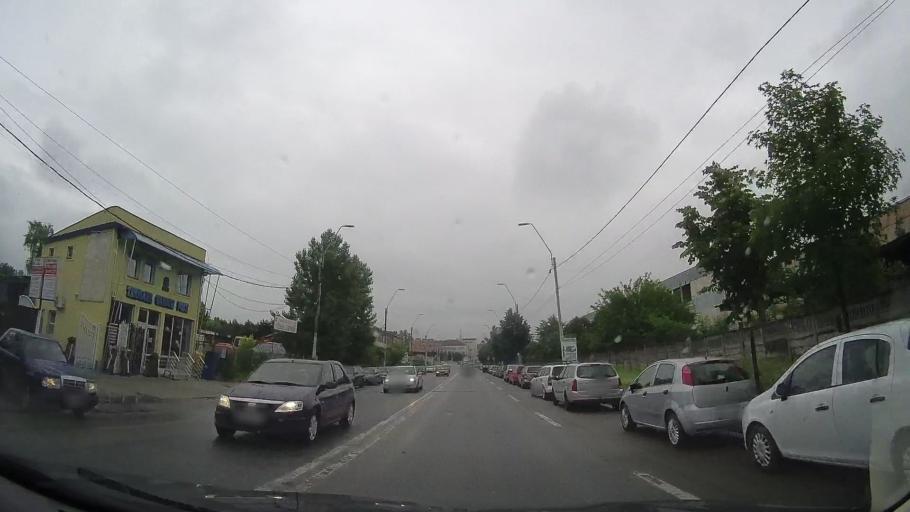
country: RO
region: Mehedinti
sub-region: Municipiul Drobeta-Turnu Severin
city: Drobeta-Turnu Severin
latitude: 44.6239
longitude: 22.6347
